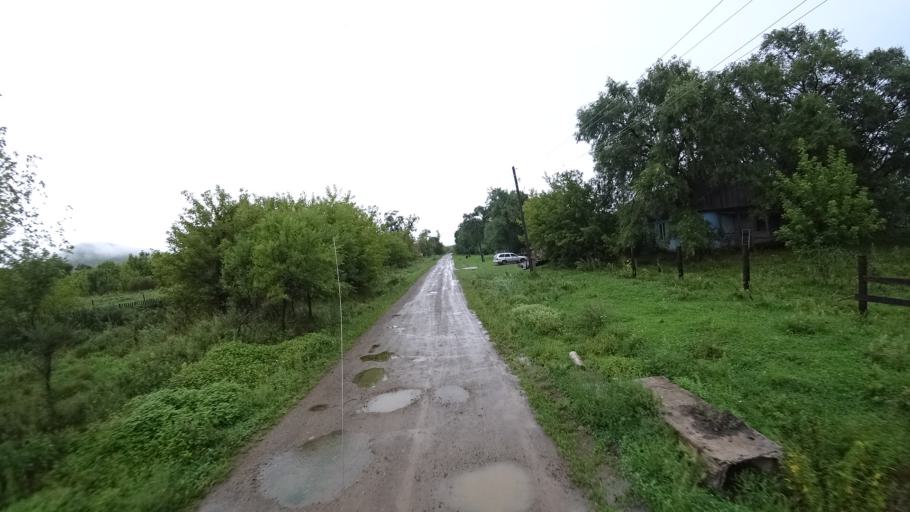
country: RU
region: Primorskiy
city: Monastyrishche
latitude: 44.2523
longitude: 132.4263
